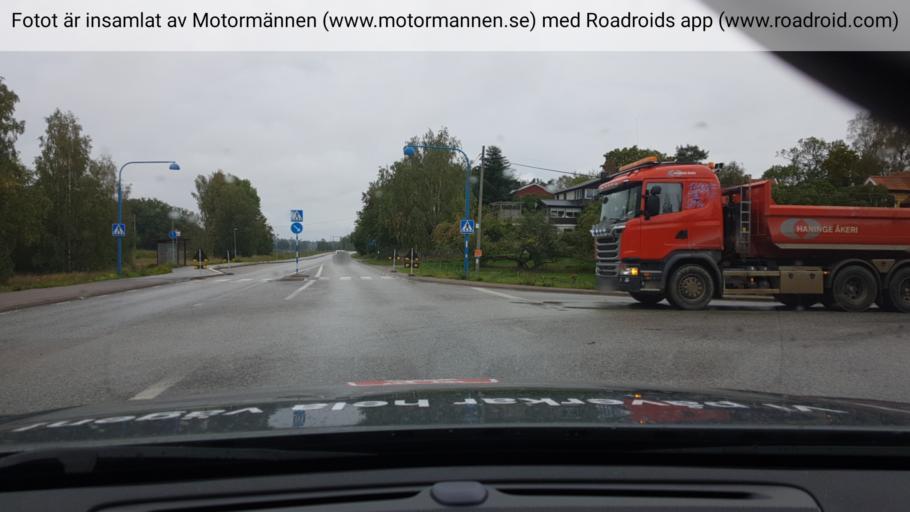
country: SE
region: Stockholm
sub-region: Nynashamns Kommun
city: Osmo
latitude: 58.9413
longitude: 17.9118
